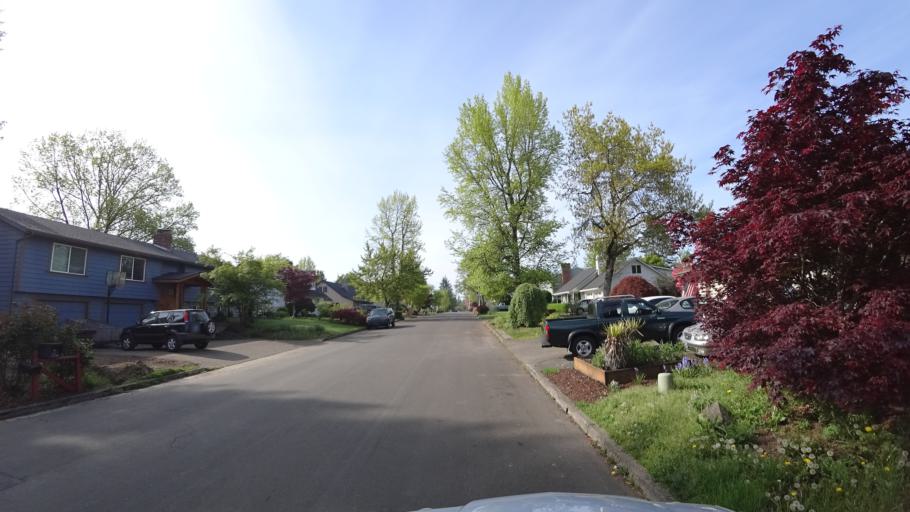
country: US
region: Oregon
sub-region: Washington County
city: Hillsboro
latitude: 45.5274
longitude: -122.9647
